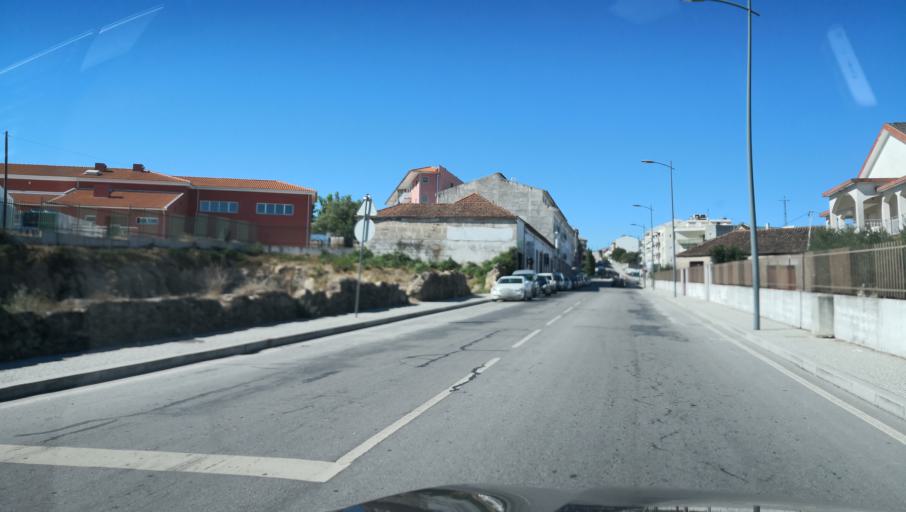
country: PT
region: Vila Real
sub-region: Valpacos
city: Valpacos
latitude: 41.6034
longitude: -7.3092
